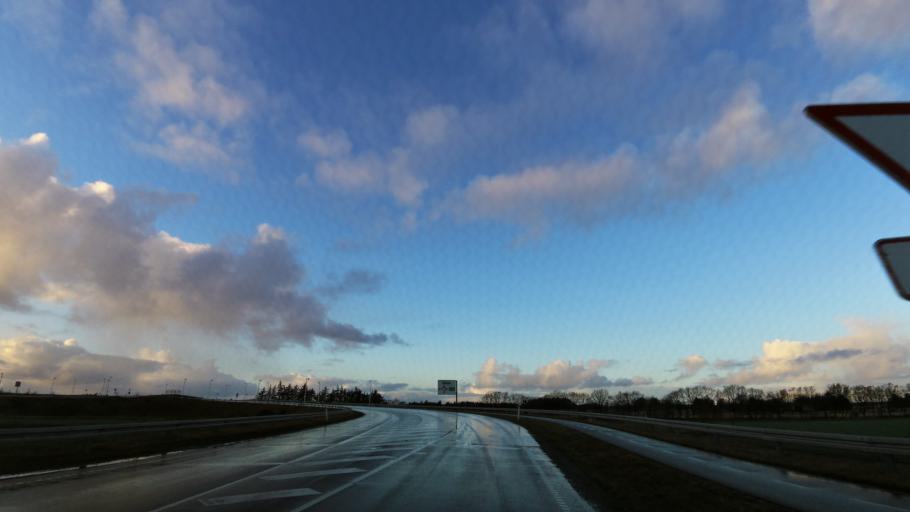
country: DK
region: Central Jutland
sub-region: Herning Kommune
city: Lind
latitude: 56.0142
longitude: 9.0289
